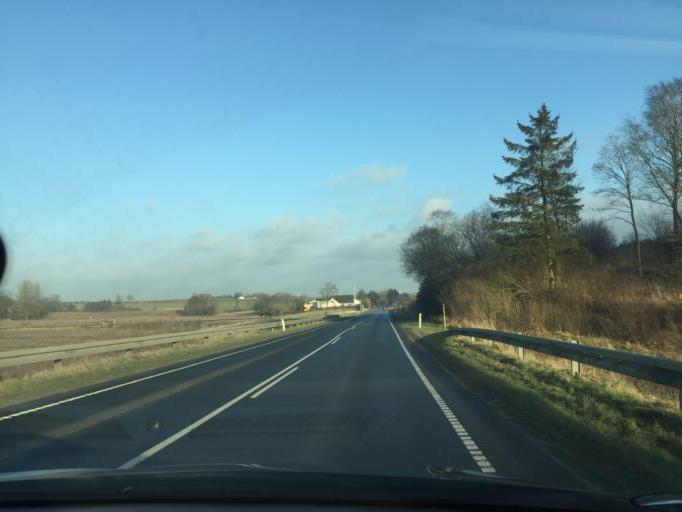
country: DK
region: South Denmark
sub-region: Faaborg-Midtfyn Kommune
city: Faaborg
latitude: 55.1943
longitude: 10.3155
